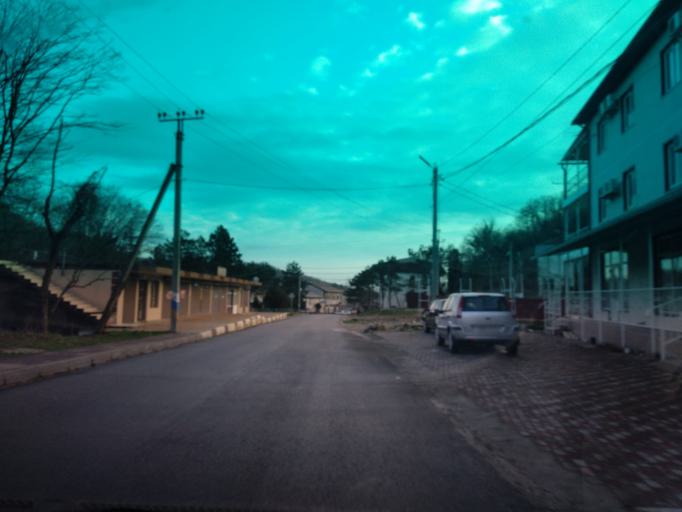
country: RU
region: Krasnodarskiy
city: Novomikhaylovskiy
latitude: 44.2634
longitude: 38.8234
